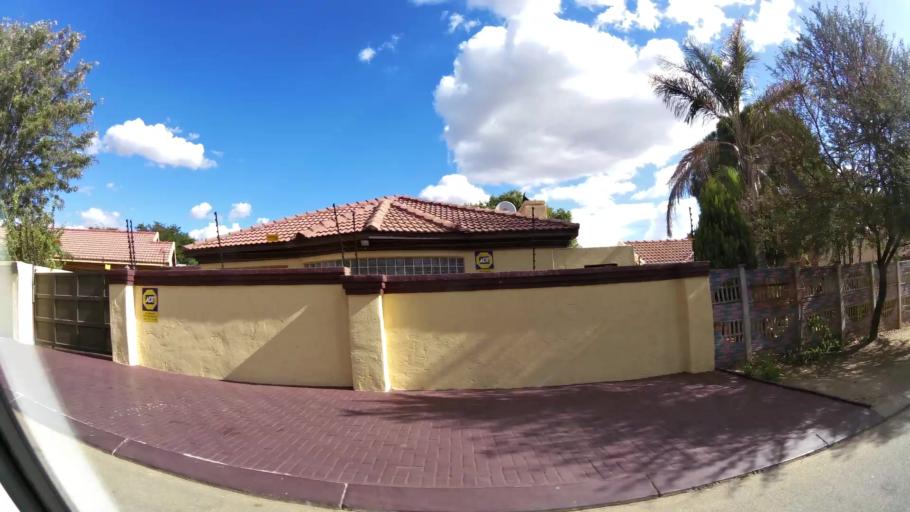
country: ZA
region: Limpopo
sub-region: Capricorn District Municipality
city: Polokwane
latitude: -23.8847
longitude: 29.4710
